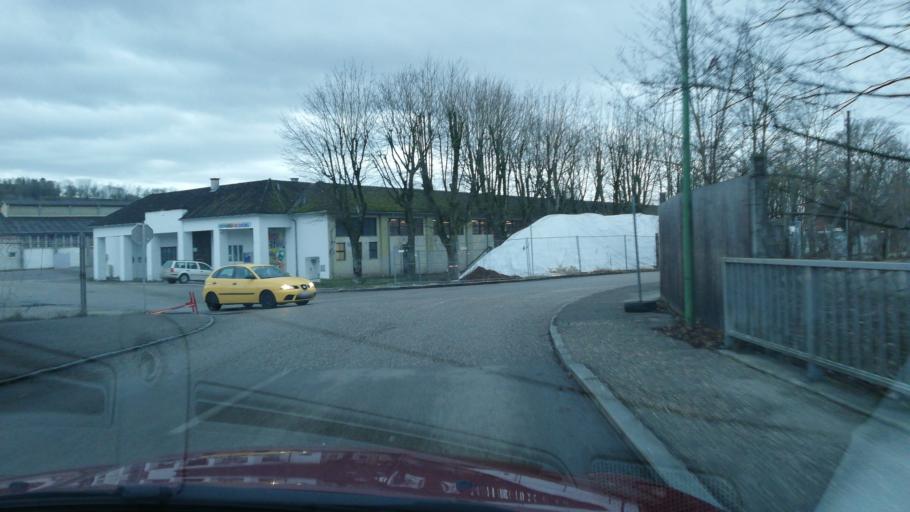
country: AT
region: Upper Austria
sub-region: Wels-Land
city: Thalheim bei Wels
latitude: 48.1526
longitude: 14.0150
